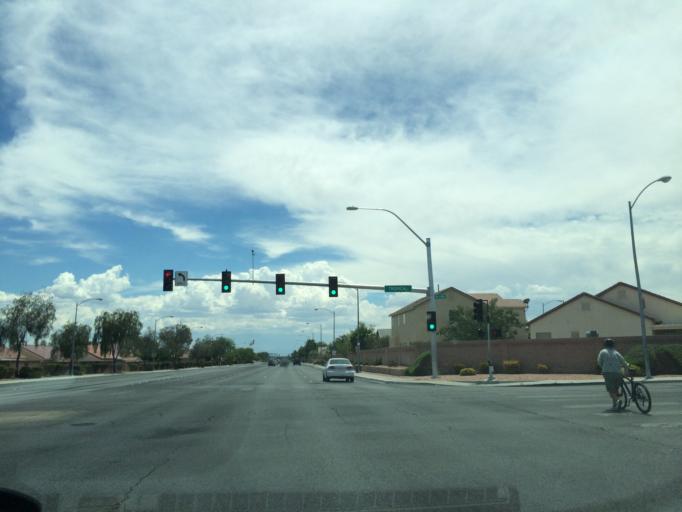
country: US
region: Nevada
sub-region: Clark County
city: North Las Vegas
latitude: 36.2693
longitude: -115.1800
